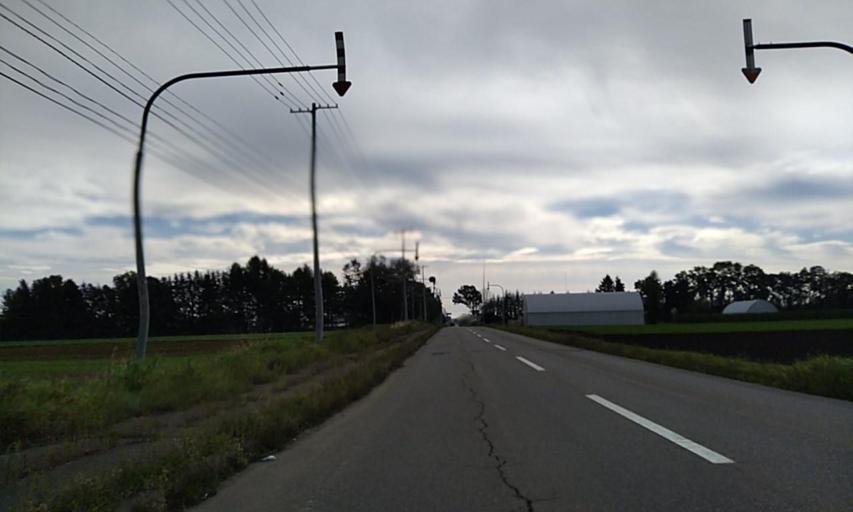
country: JP
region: Hokkaido
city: Obihiro
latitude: 42.8551
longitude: 143.1528
